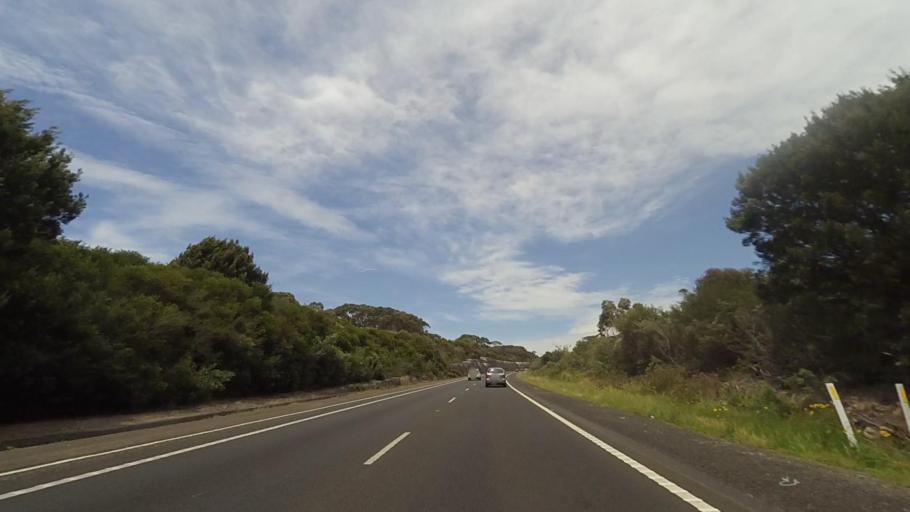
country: AU
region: New South Wales
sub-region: Wollongong
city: Helensburgh
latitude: -34.2378
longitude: 150.9463
